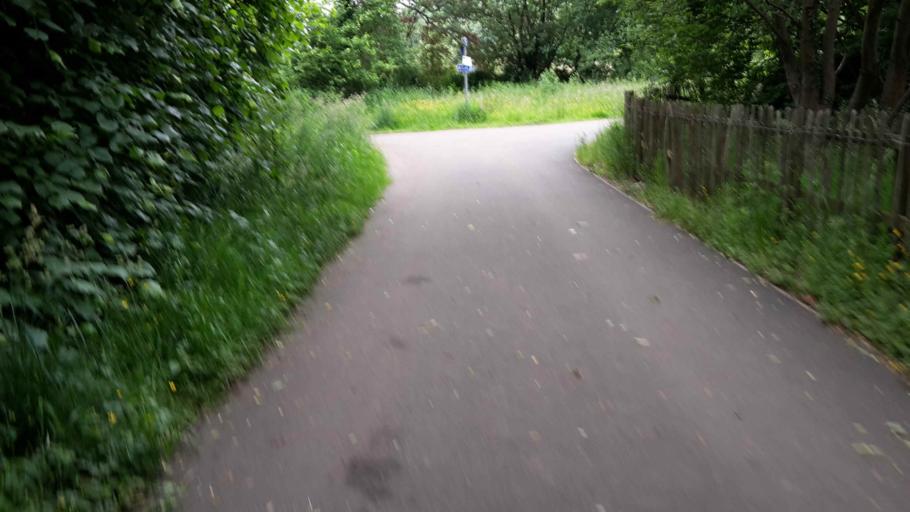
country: GB
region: Scotland
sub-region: South Lanarkshire
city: Uddingston
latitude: 55.8219
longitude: -4.0929
